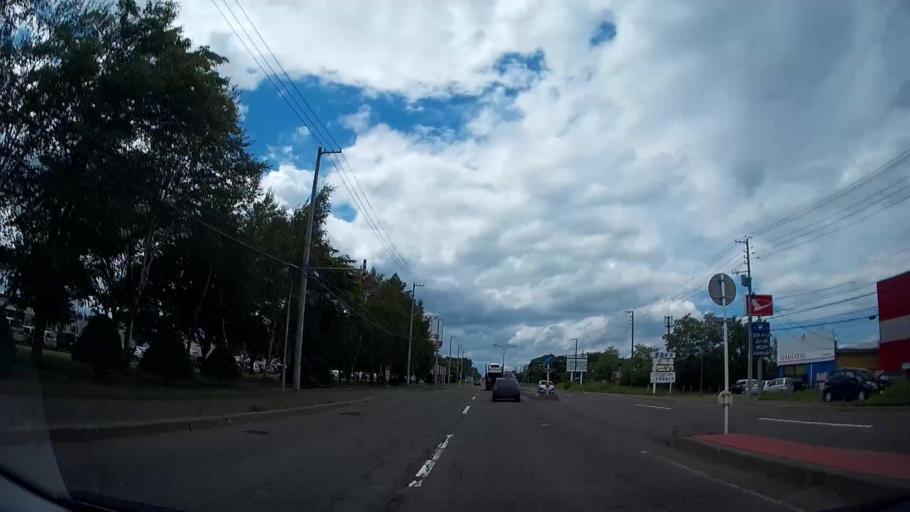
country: JP
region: Hokkaido
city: Chitose
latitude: 42.8657
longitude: 141.5943
